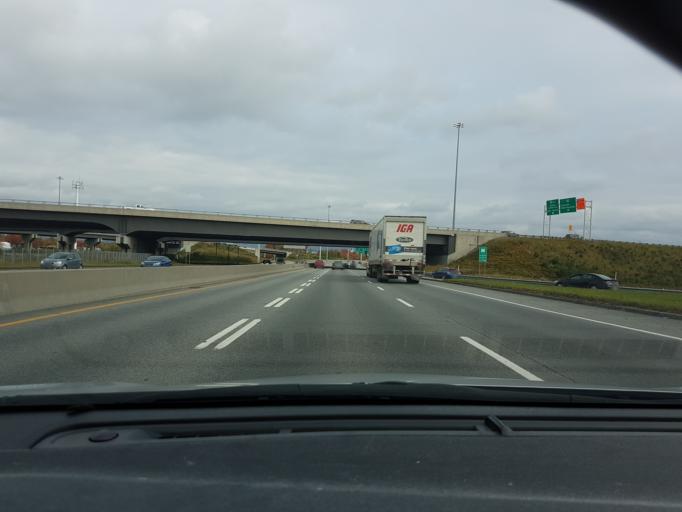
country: CA
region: Quebec
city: L'Ancienne-Lorette
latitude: 46.7931
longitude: -71.2884
